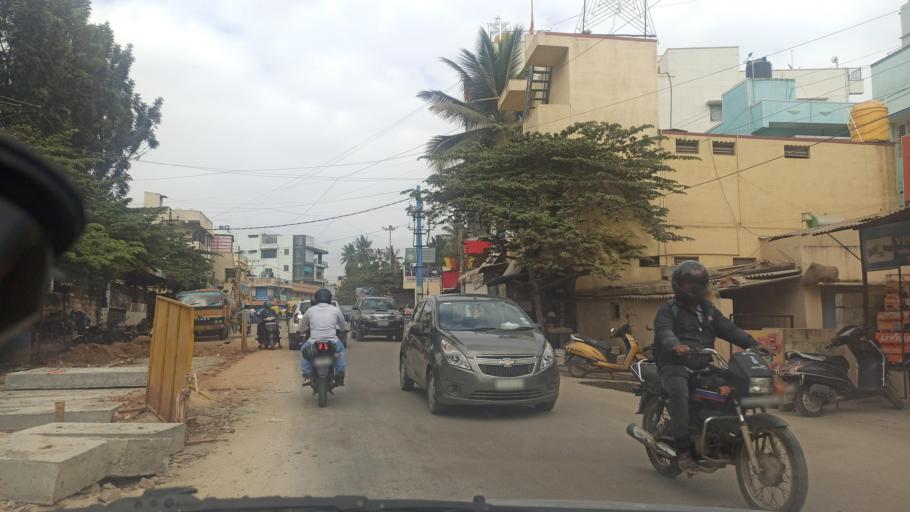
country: IN
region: Karnataka
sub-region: Bangalore Urban
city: Yelahanka
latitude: 13.0484
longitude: 77.6122
